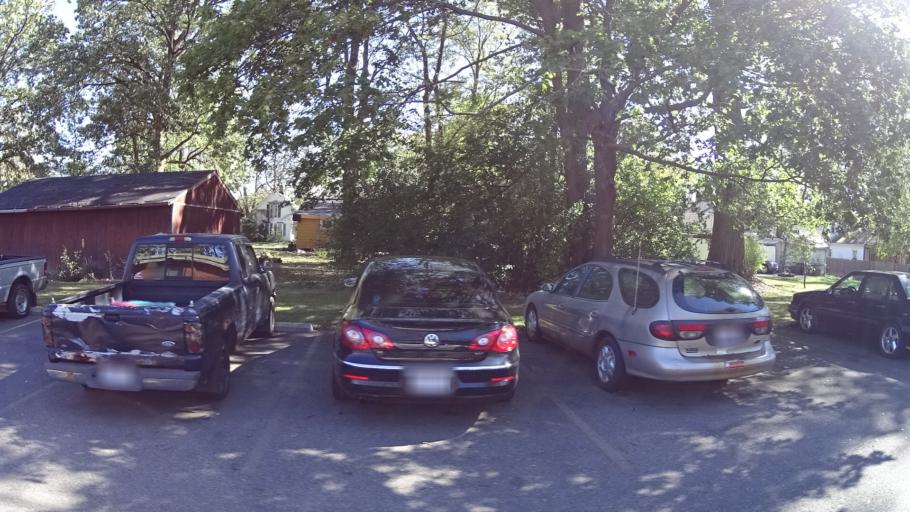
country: US
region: Ohio
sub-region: Lorain County
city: Oberlin
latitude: 41.2936
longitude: -82.2131
